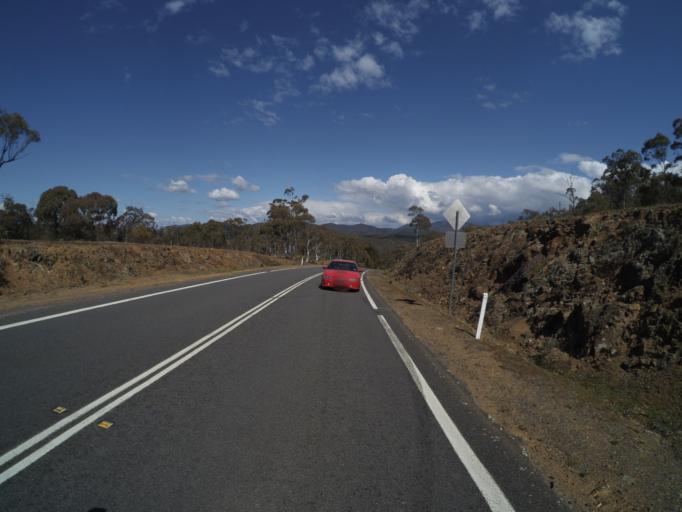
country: AU
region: Australian Capital Territory
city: Macquarie
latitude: -35.3154
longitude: 148.9490
